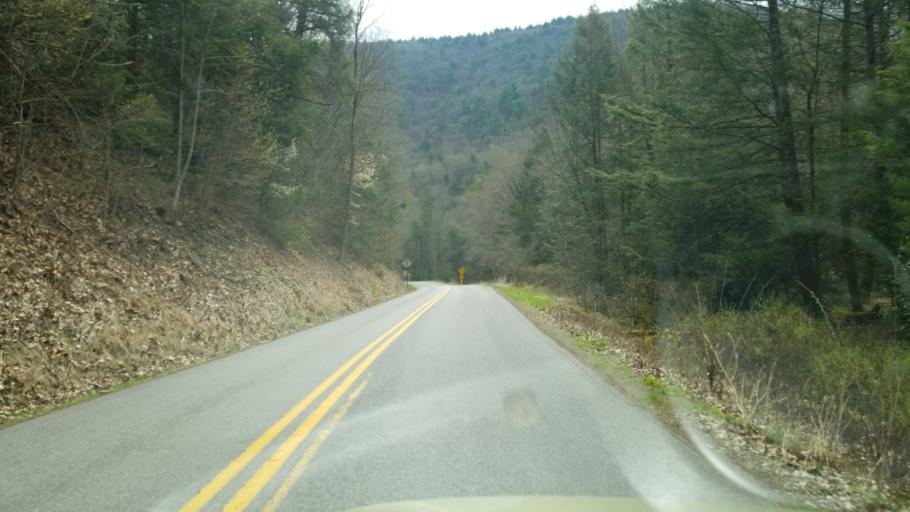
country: US
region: Pennsylvania
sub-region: Cameron County
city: Emporium
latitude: 41.2832
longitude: -78.1292
